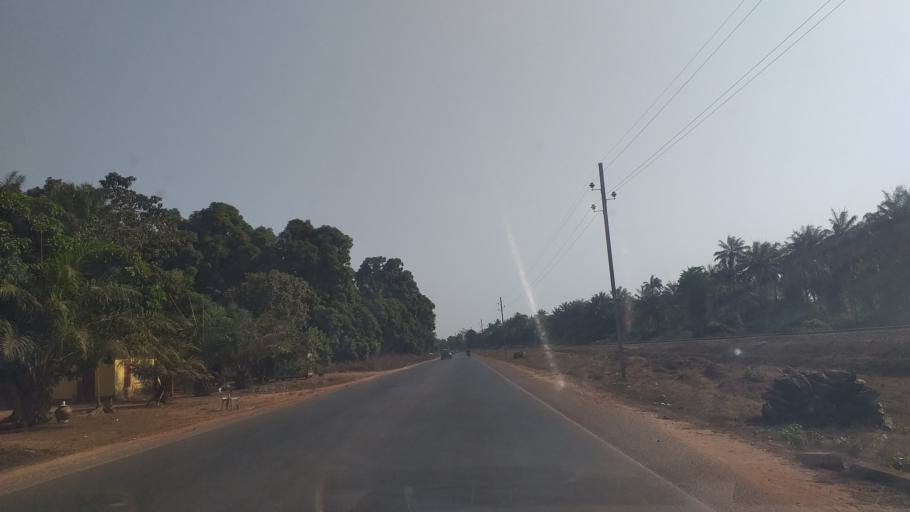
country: GN
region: Boke
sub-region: Boke Prefecture
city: Kamsar
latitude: 10.7415
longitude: -14.5127
